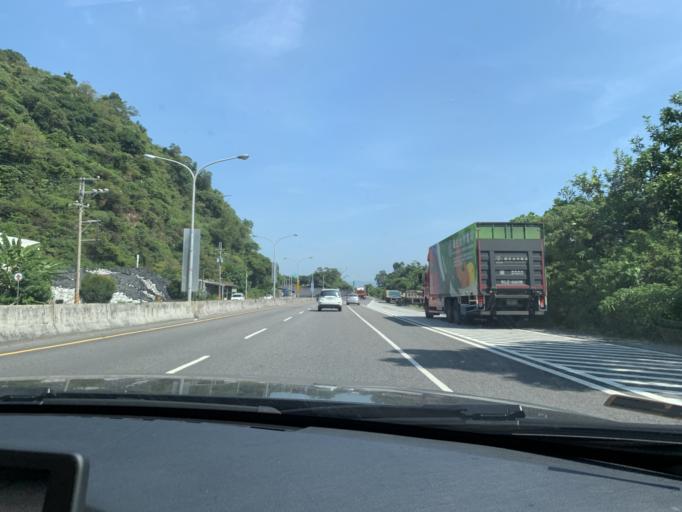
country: TW
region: Taiwan
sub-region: Yilan
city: Yilan
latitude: 24.6112
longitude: 121.8258
